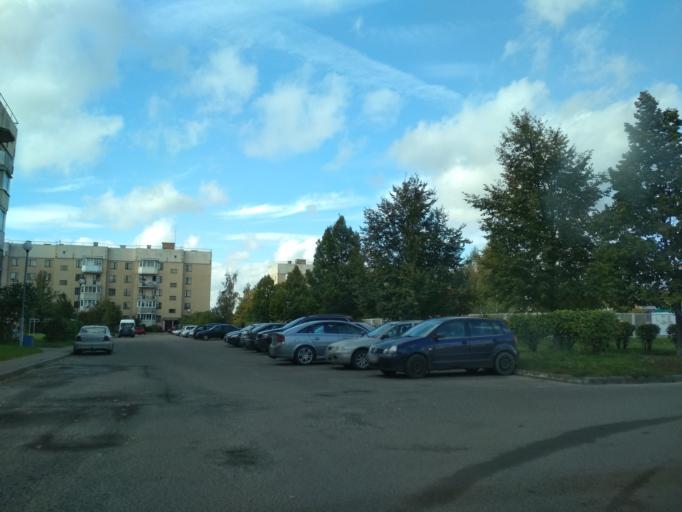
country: BY
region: Minsk
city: Mar''ina Horka
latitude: 53.5028
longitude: 28.1605
